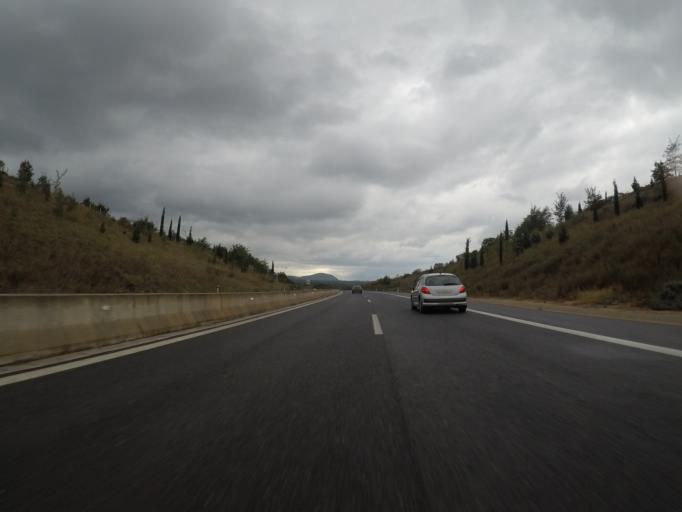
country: GR
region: Peloponnese
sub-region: Nomos Arkadias
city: Megalopoli
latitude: 37.3584
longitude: 22.1275
